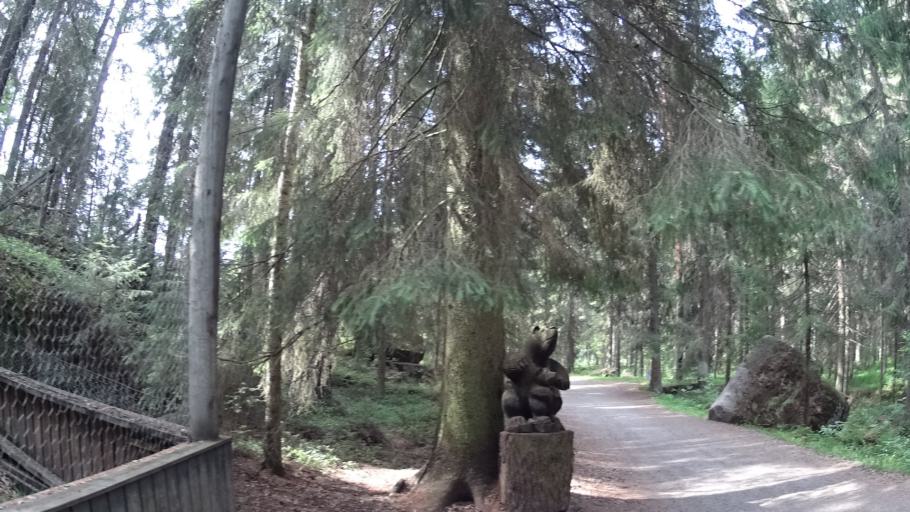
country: FI
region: Southern Ostrobothnia
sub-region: Kuusiokunnat
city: AEhtaeri
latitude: 62.5391
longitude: 24.1792
